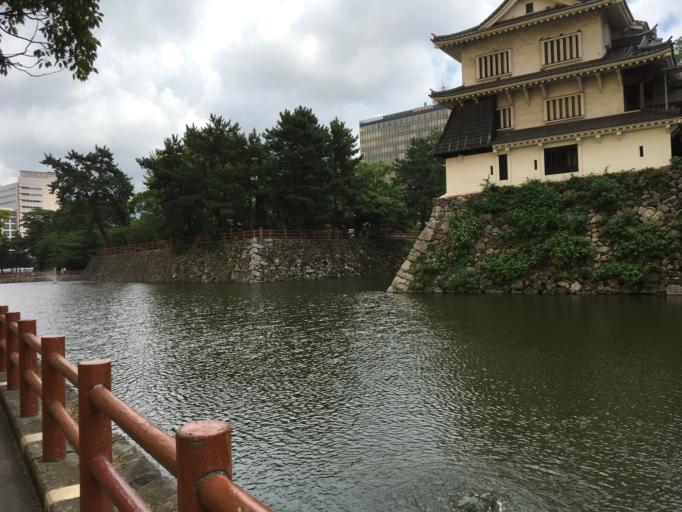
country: JP
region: Fukuoka
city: Kitakyushu
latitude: 33.8857
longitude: 130.8742
